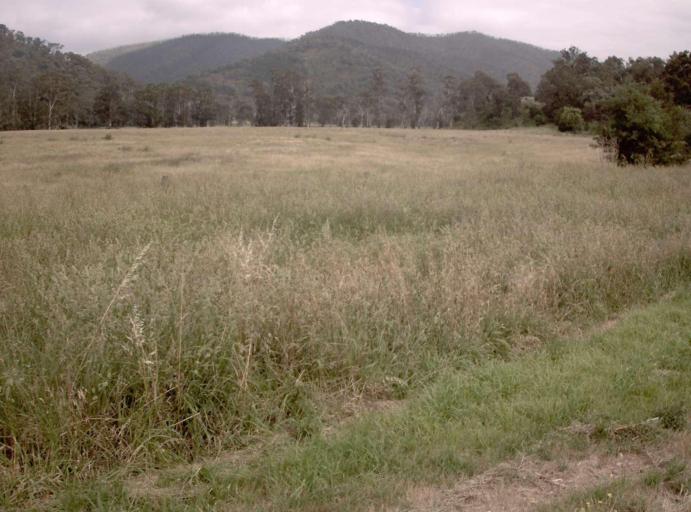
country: AU
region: Victoria
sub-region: Wellington
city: Heyfield
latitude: -37.7596
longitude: 146.6692
